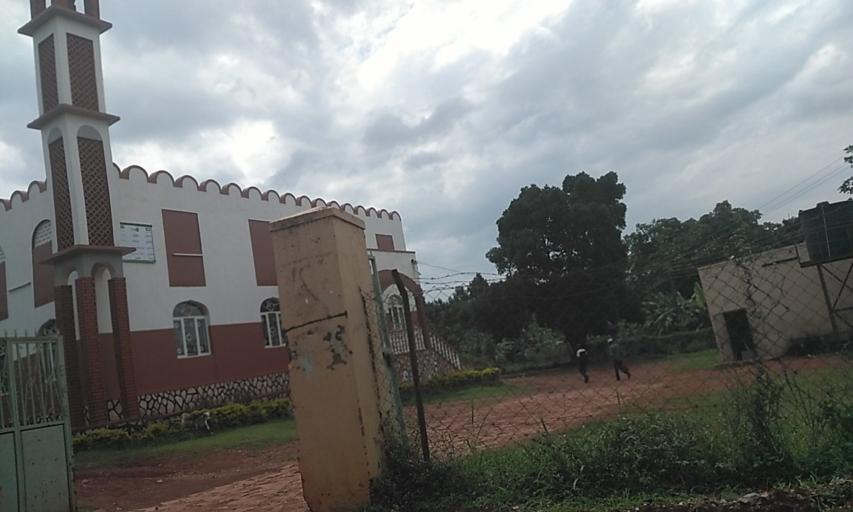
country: UG
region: Central Region
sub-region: Wakiso District
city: Kireka
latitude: 0.3527
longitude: 32.6264
